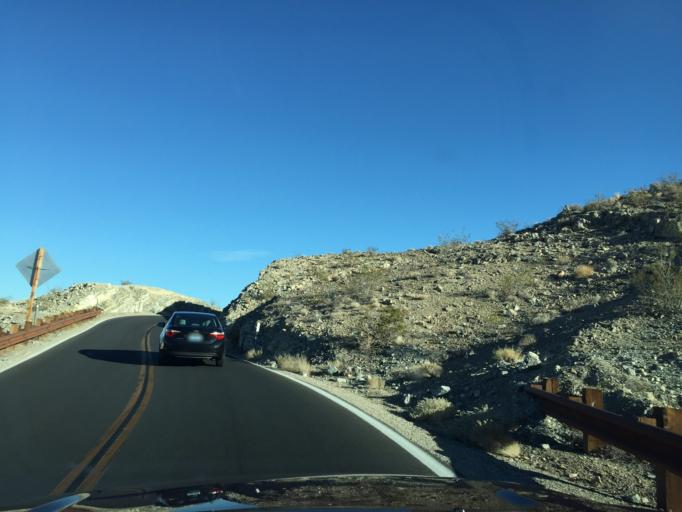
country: US
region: California
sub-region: Inyo County
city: Lone Pine
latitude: 36.3516
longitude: -117.5361
